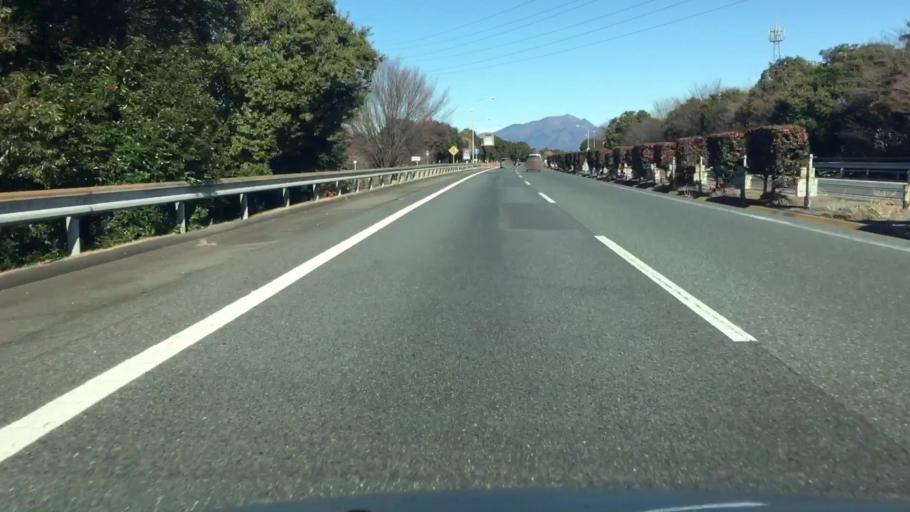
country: JP
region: Gunma
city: Kanekomachi
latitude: 36.4310
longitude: 139.0149
